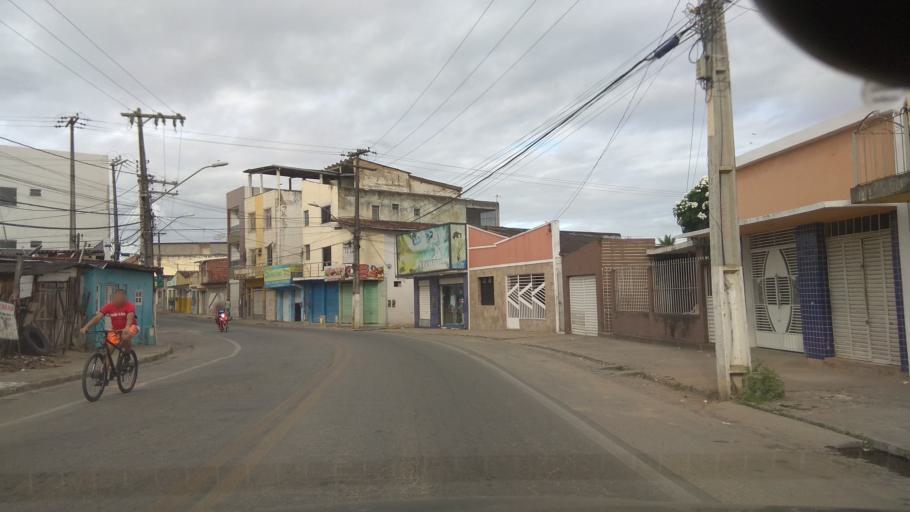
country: BR
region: Bahia
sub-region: Ipiau
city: Ipiau
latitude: -14.1360
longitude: -39.7415
